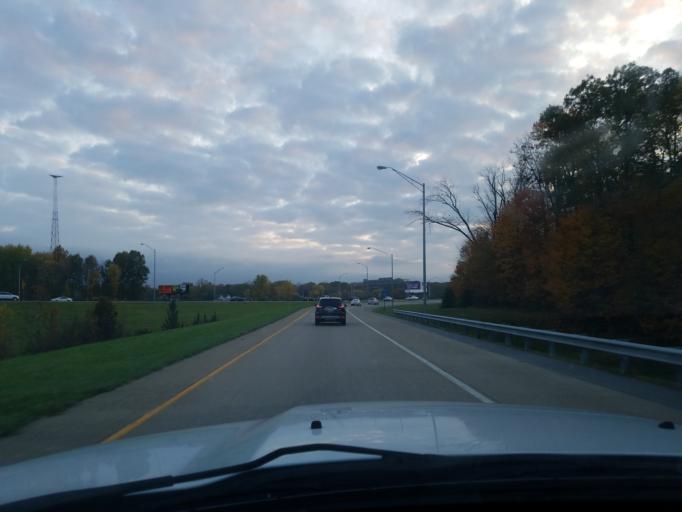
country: US
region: Indiana
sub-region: Clark County
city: Clarksville
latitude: 38.3469
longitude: -85.7583
